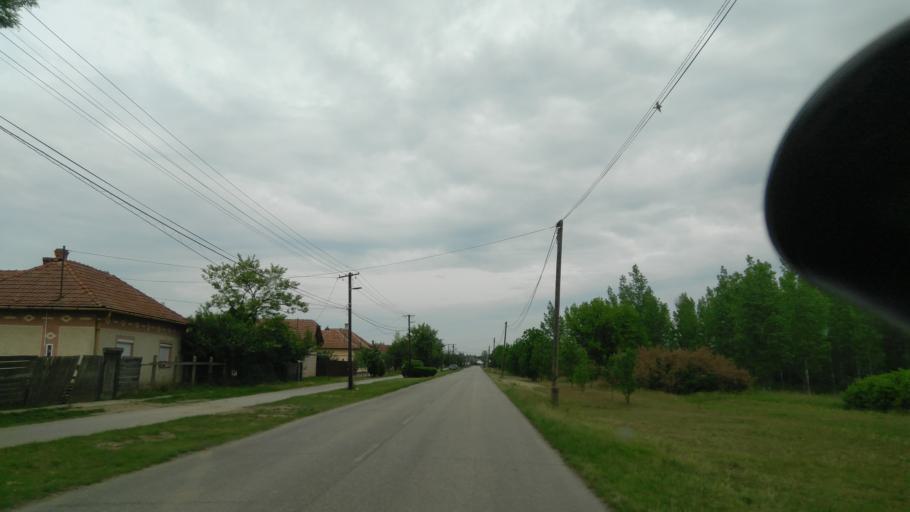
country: HU
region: Bekes
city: Veszto
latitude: 46.9171
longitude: 21.2545
